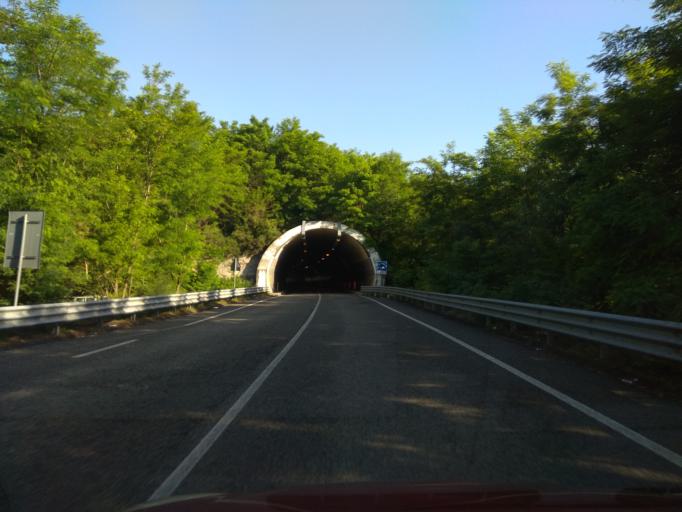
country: IT
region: Piedmont
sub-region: Provincia di Biella
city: Vallanzengo
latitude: 45.6052
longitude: 8.1653
